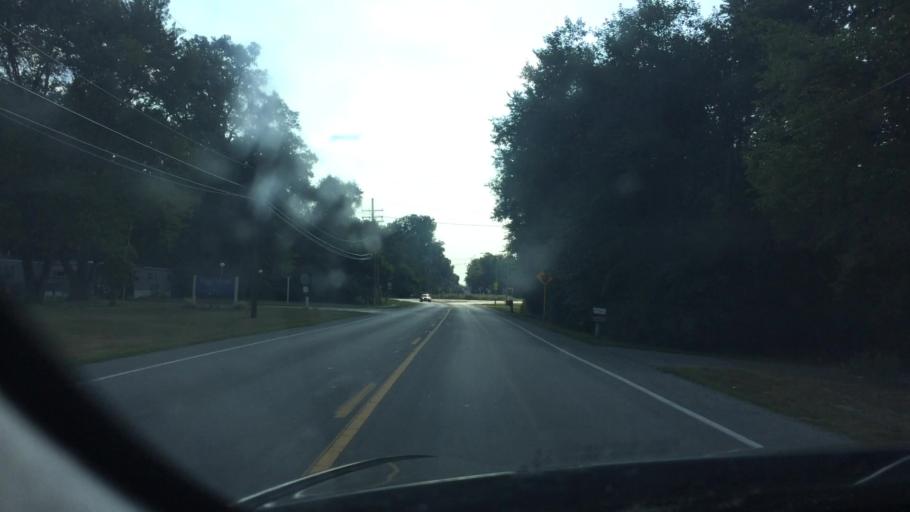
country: US
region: Ohio
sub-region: Lucas County
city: Holland
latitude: 41.6539
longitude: -83.7206
